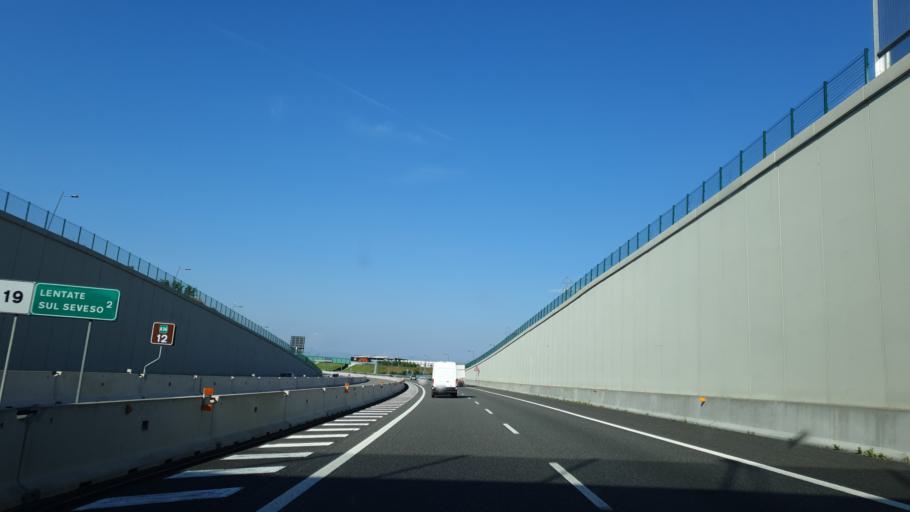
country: IT
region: Lombardy
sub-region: Provincia di Como
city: San Michele-San Giorgio
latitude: 45.6794
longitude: 9.0661
